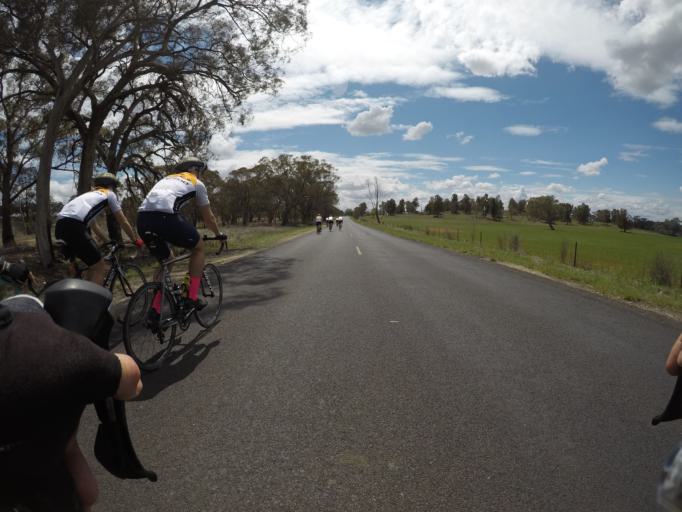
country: AU
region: New South Wales
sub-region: Dubbo Municipality
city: Dubbo
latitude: -32.2913
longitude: 148.5985
